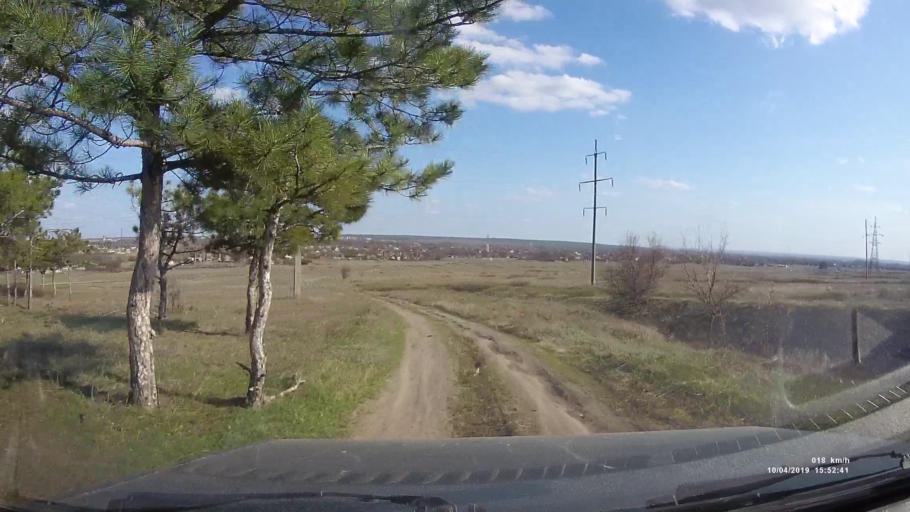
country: RU
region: Rostov
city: Masalovka
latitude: 48.4193
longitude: 40.2571
